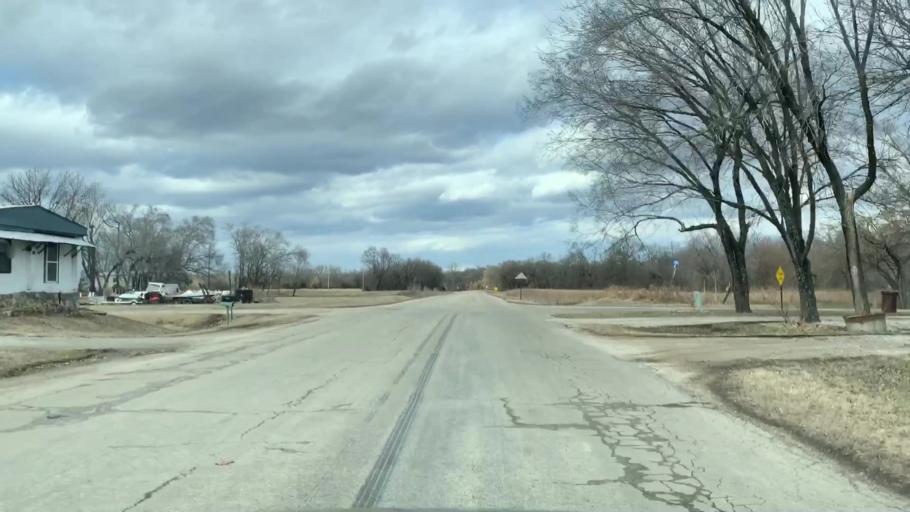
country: US
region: Kansas
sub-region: Neosho County
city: Chanute
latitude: 37.7453
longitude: -95.4704
